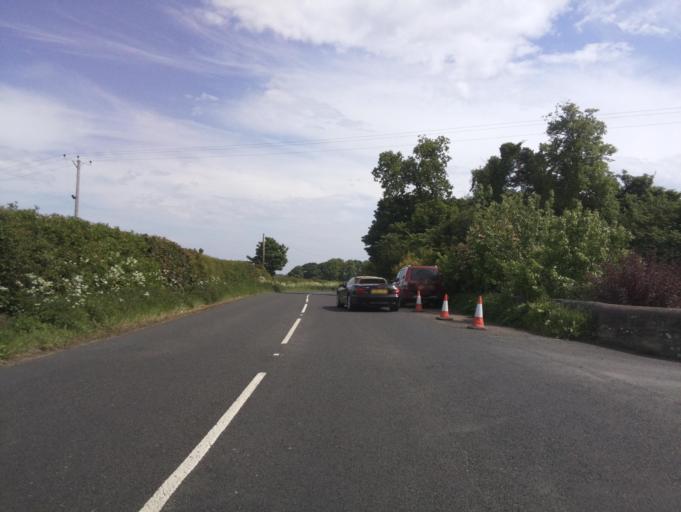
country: GB
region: England
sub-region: Northumberland
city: Alnwick
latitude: 55.4298
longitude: -1.7045
